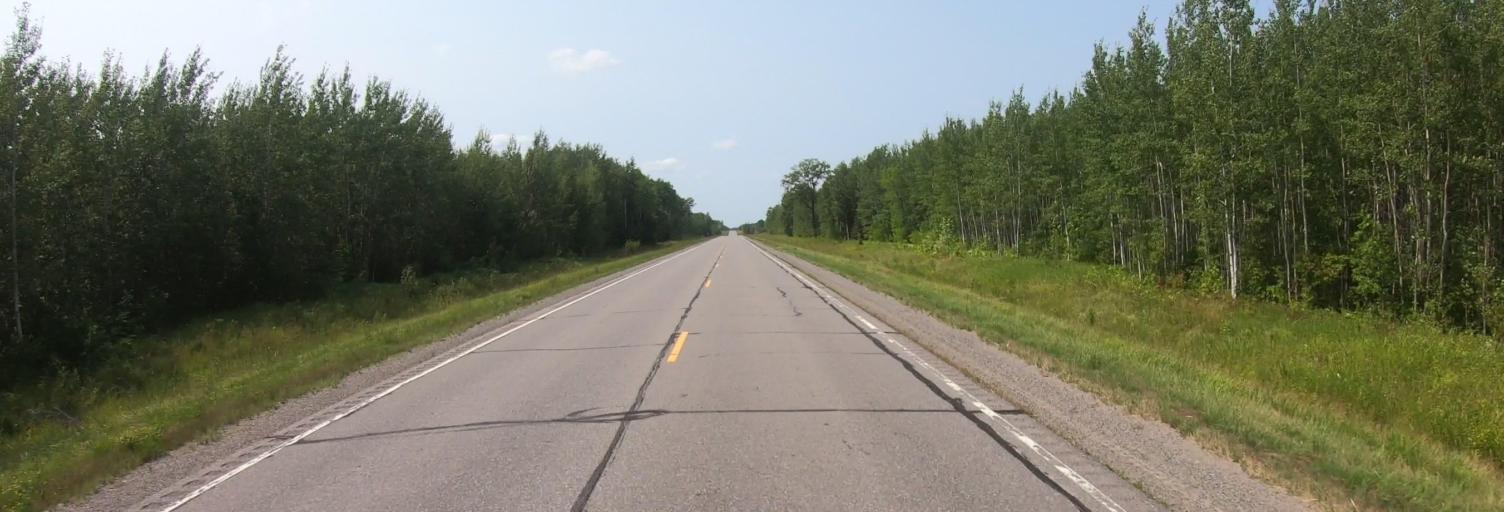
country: US
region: Minnesota
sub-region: Lake of the Woods County
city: Baudette
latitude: 48.6995
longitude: -94.3577
